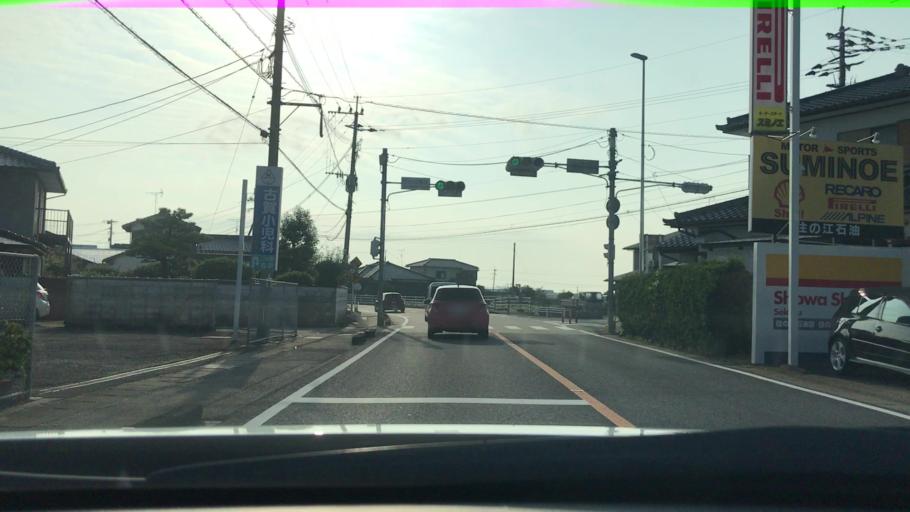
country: JP
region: Saga Prefecture
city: Saga-shi
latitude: 33.2007
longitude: 130.2005
